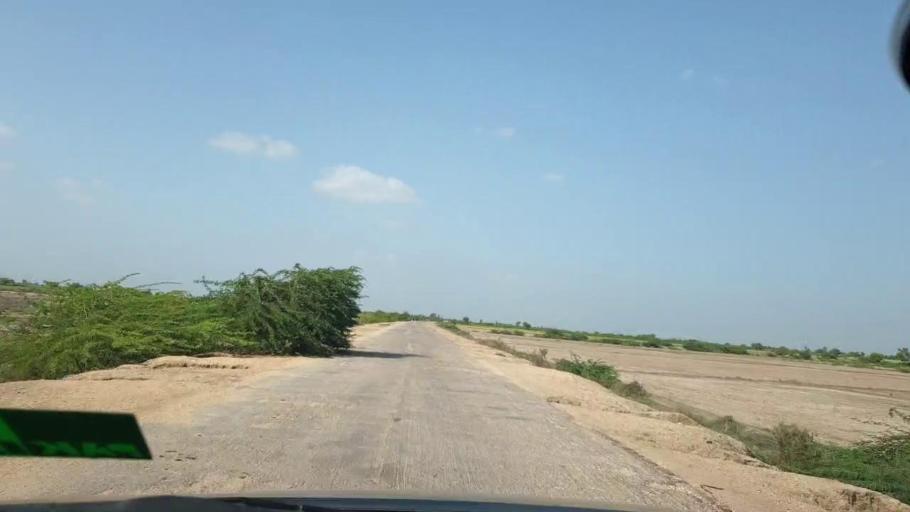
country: PK
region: Sindh
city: Tando Bago
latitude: 24.6979
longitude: 69.1902
